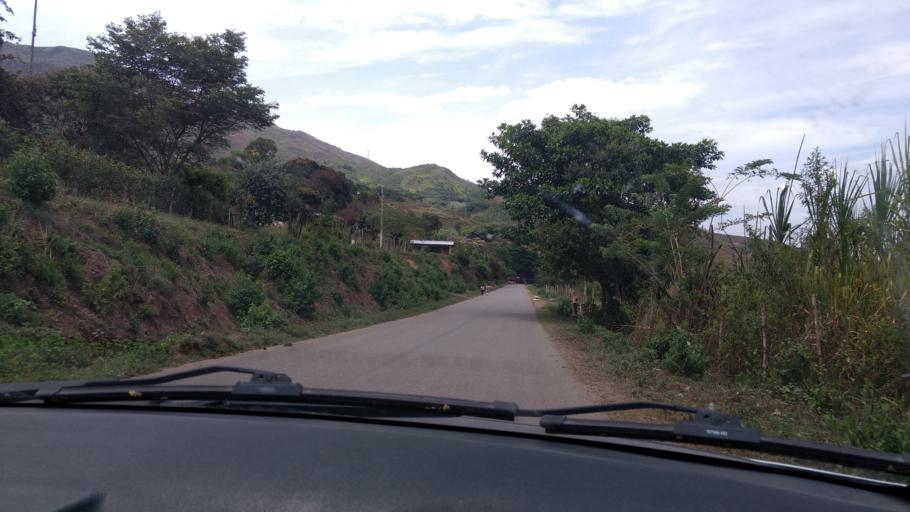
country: CO
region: Cauca
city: Buenos Aires
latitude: 3.0359
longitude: -76.6722
